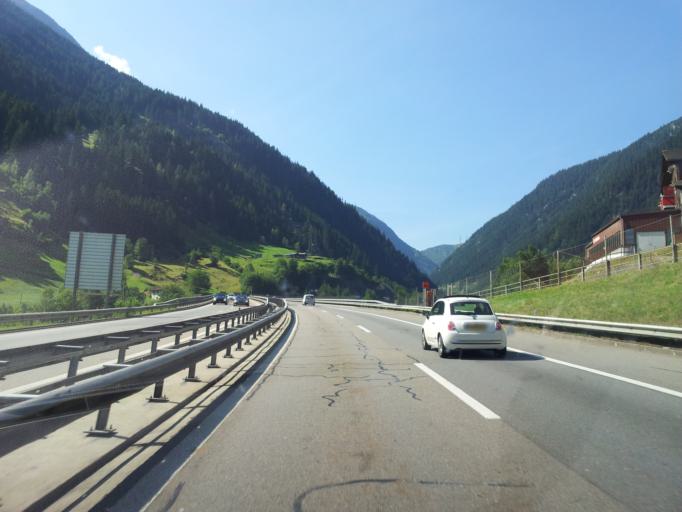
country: CH
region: Uri
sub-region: Uri
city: Andermatt
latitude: 46.6984
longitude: 8.5964
